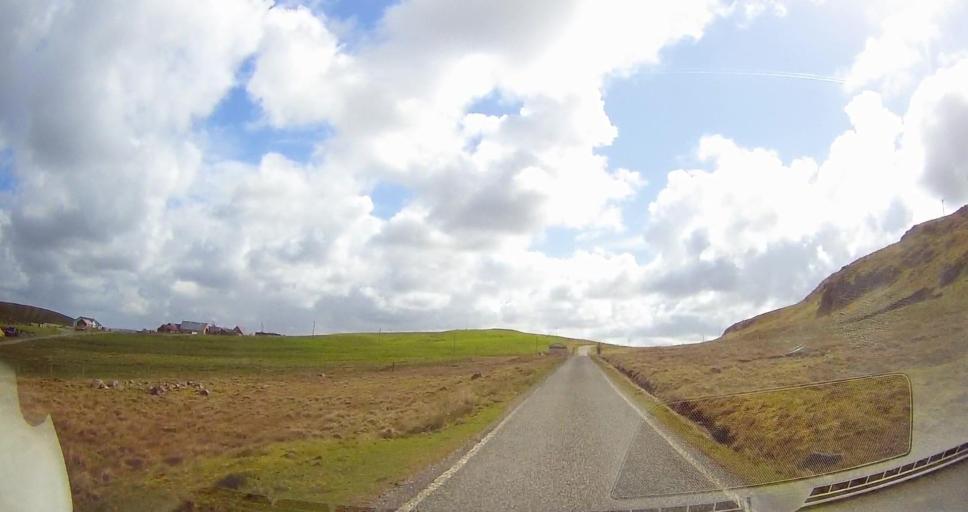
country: GB
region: Scotland
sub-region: Shetland Islands
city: Lerwick
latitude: 60.5466
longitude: -1.3405
